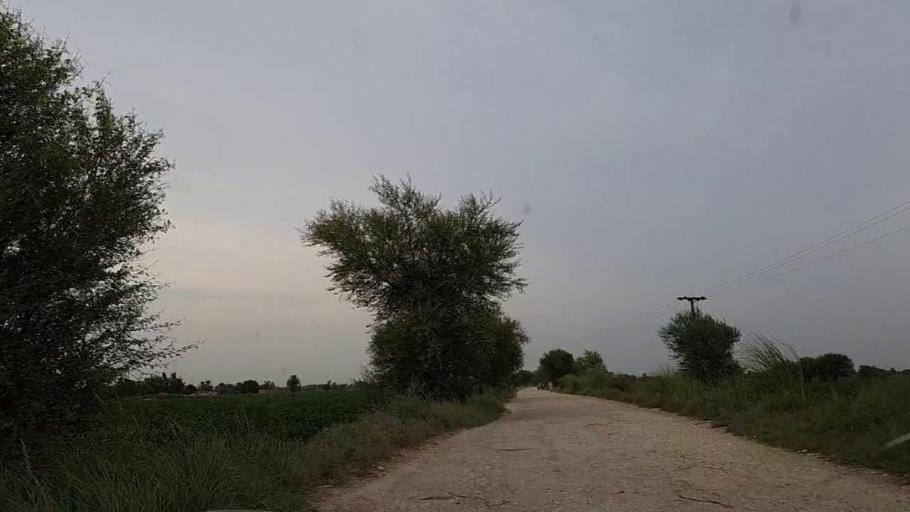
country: PK
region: Sindh
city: Mirpur Mathelo
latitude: 27.8552
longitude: 69.6317
